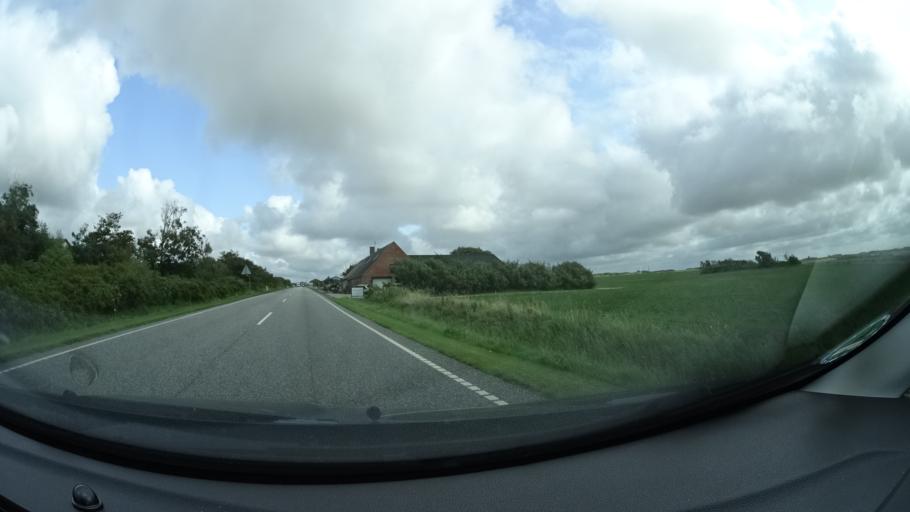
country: DK
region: Central Jutland
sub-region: Lemvig Kommune
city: Harboore
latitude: 56.5553
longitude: 8.2258
